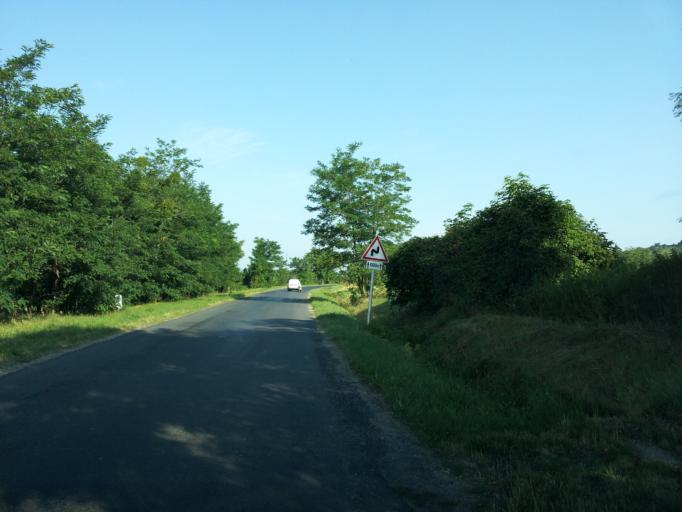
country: HU
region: Zala
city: Gyenesdias
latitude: 46.8548
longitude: 17.3280
